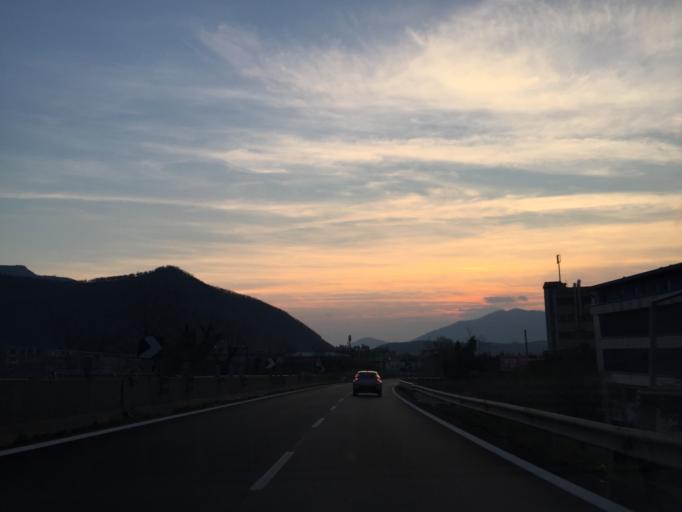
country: IT
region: Campania
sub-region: Provincia di Avellino
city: Solofra
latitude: 40.8343
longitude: 14.8373
